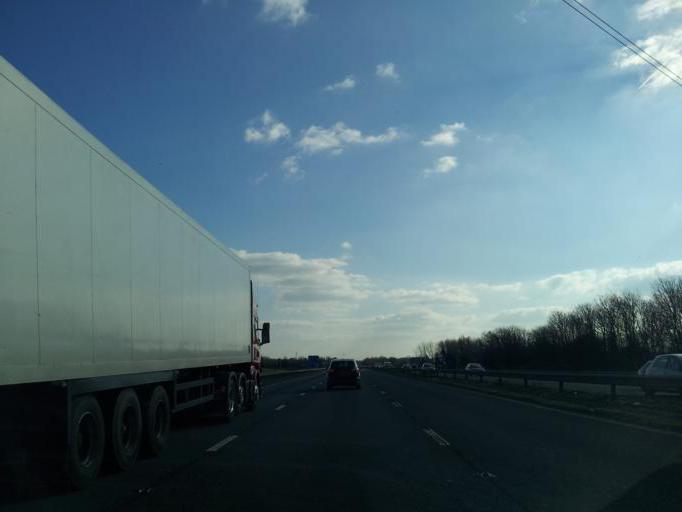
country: GB
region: England
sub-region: Somerset
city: Puriton
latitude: 51.1808
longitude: -2.9759
